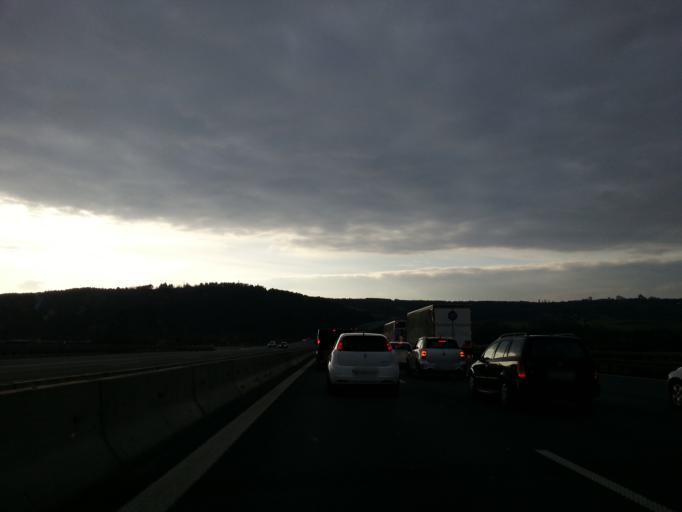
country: DE
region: Bavaria
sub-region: Regierungsbezirk Unterfranken
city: Eibelstadt
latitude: 49.7394
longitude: 9.9988
